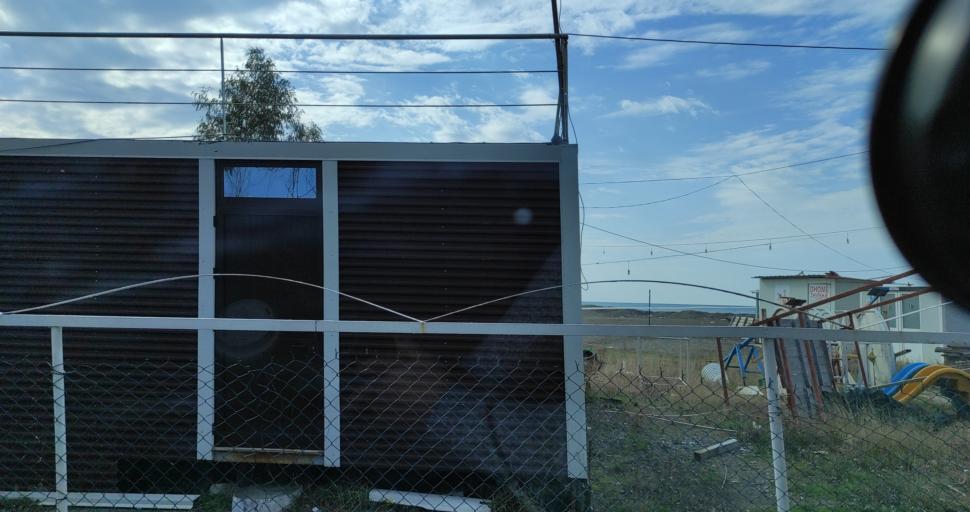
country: AL
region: Lezhe
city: Shengjin
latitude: 41.7781
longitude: 19.6033
